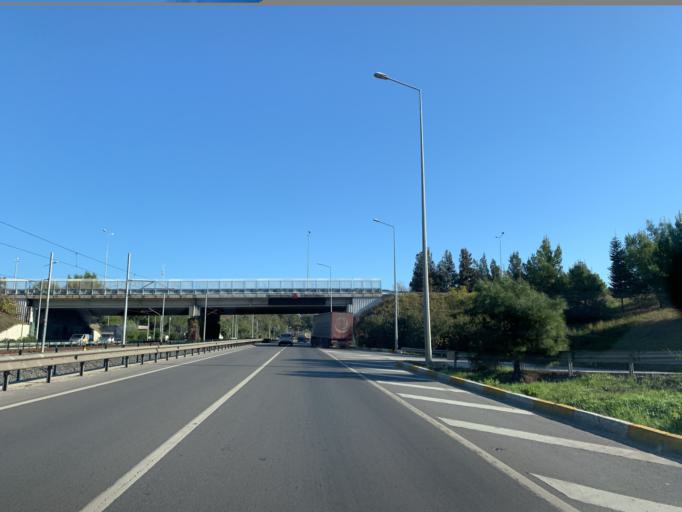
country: TR
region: Antalya
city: Aksu
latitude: 36.9444
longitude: 30.8301
